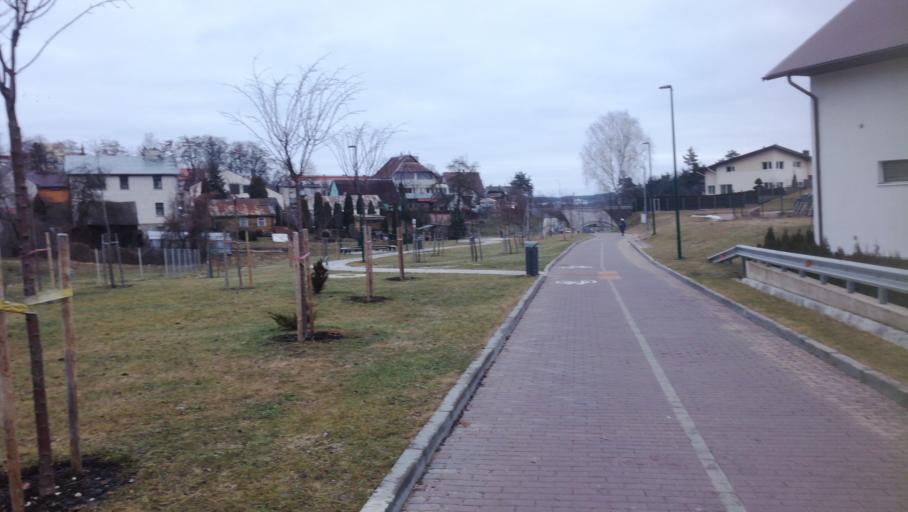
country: LT
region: Alytaus apskritis
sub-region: Alytus
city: Alytus
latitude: 54.3964
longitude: 24.0395
